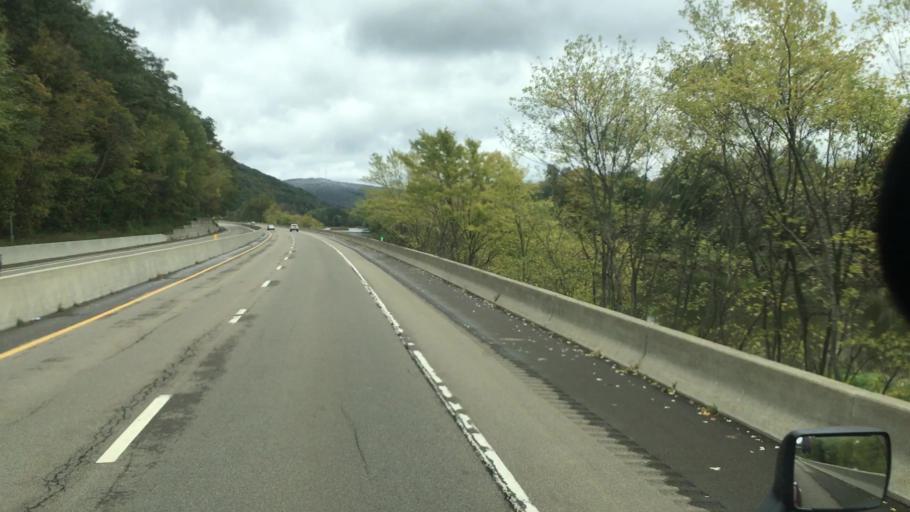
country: US
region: New York
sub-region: Cattaraugus County
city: Salamanca
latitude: 42.1165
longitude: -78.6633
